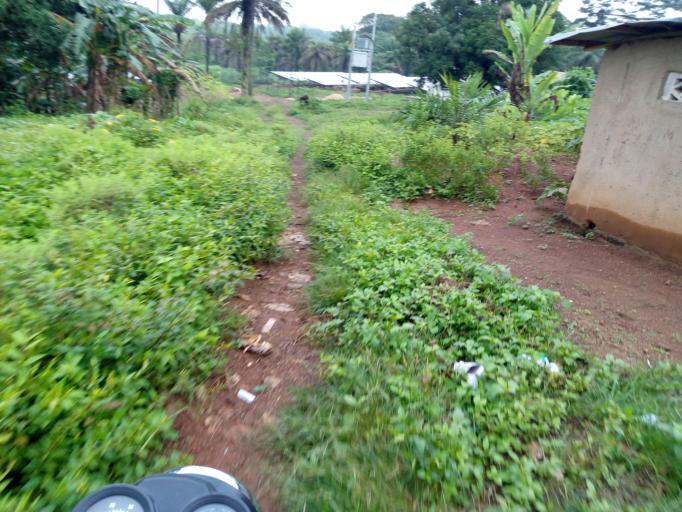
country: SL
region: Eastern Province
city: Buedu
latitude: 8.4677
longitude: -10.3432
